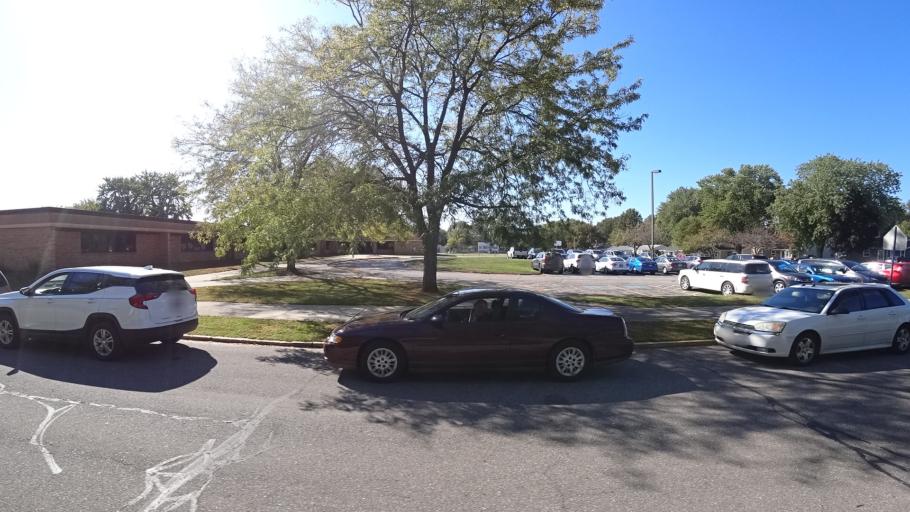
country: US
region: Indiana
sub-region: LaPorte County
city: Michigan City
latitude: 41.6963
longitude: -86.9060
